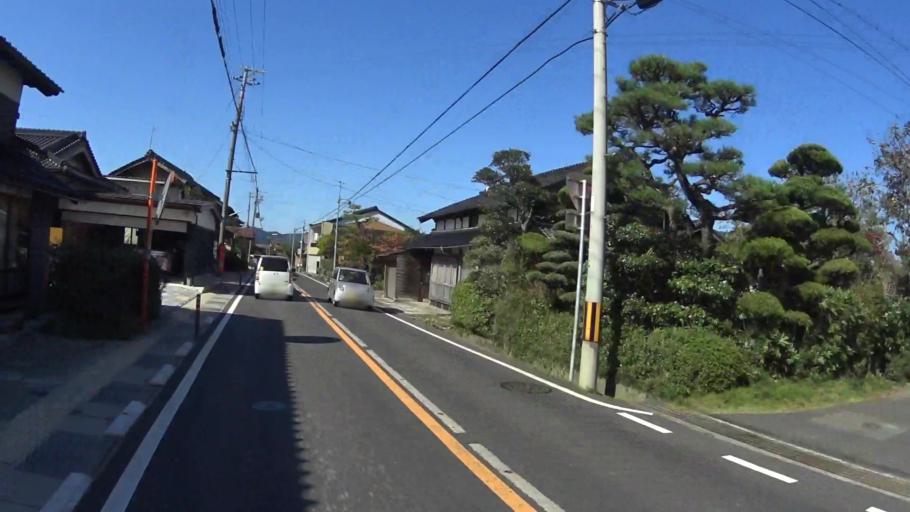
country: JP
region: Hyogo
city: Toyooka
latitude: 35.5821
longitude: 134.9630
